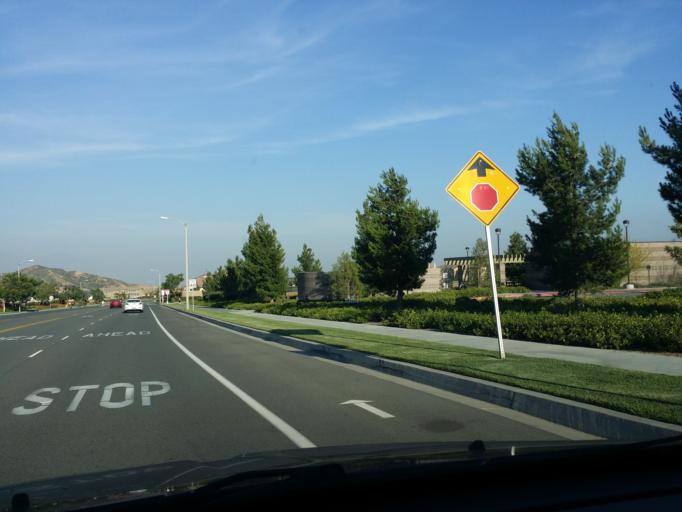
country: US
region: California
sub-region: San Bernardino County
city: Muscoy
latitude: 34.1890
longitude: -117.4149
